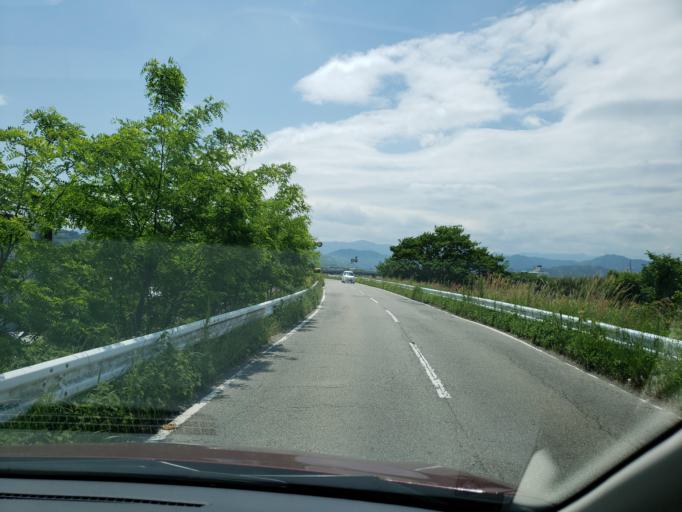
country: JP
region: Tokushima
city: Tokushima-shi
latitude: 34.0794
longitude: 134.5025
